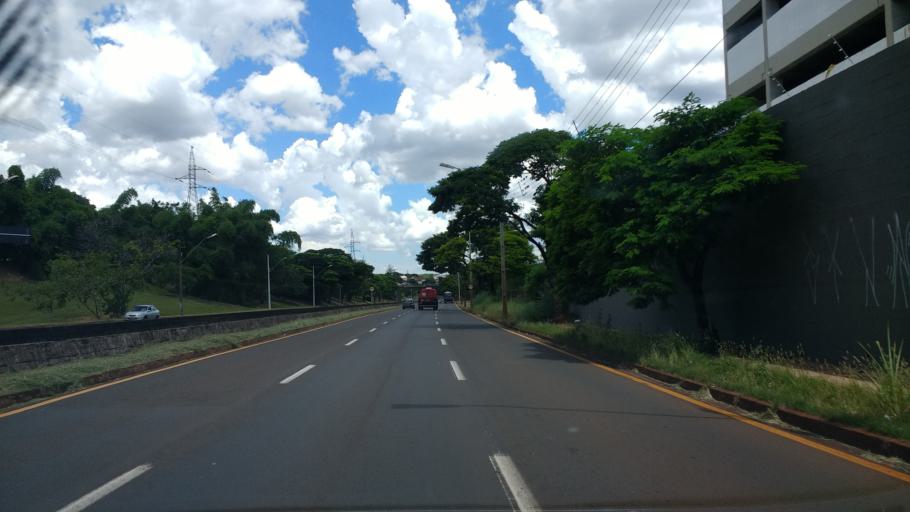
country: BR
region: Parana
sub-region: Londrina
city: Londrina
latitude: -23.3233
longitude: -51.1479
